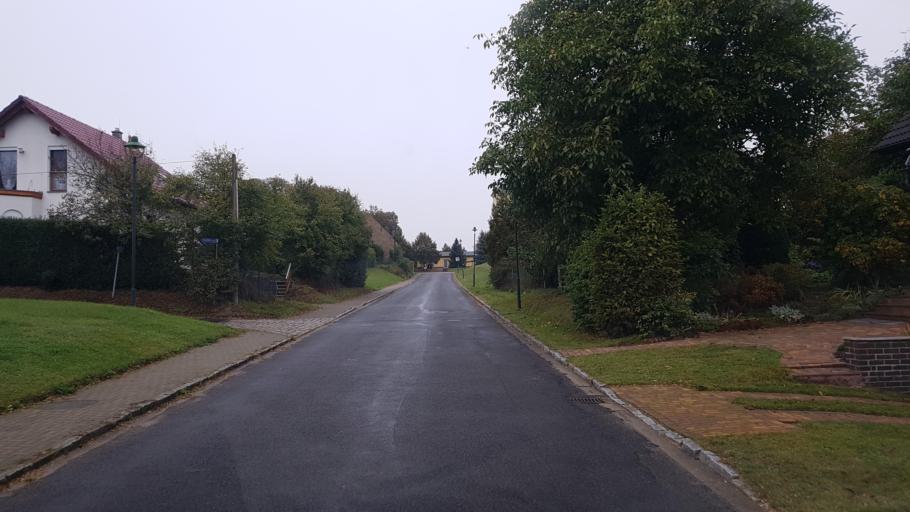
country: DE
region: Brandenburg
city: Furstenwalde
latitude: 52.4325
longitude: 14.0169
